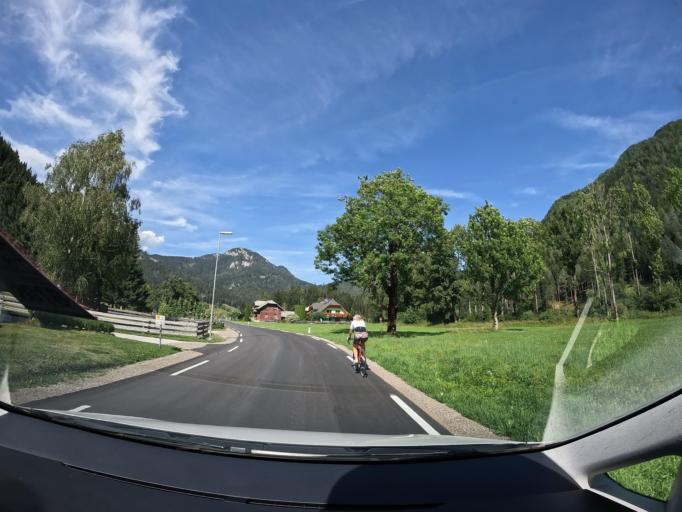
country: AT
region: Carinthia
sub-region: Politischer Bezirk Feldkirchen
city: Feldkirchen in Karnten
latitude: 46.6901
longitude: 14.1217
